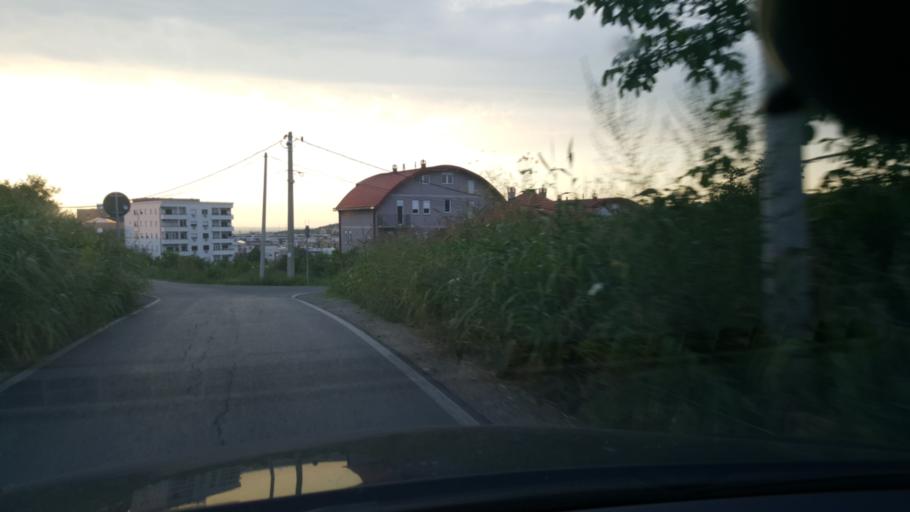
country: RS
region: Central Serbia
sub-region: Belgrade
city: Zvezdara
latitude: 44.7839
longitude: 20.5325
